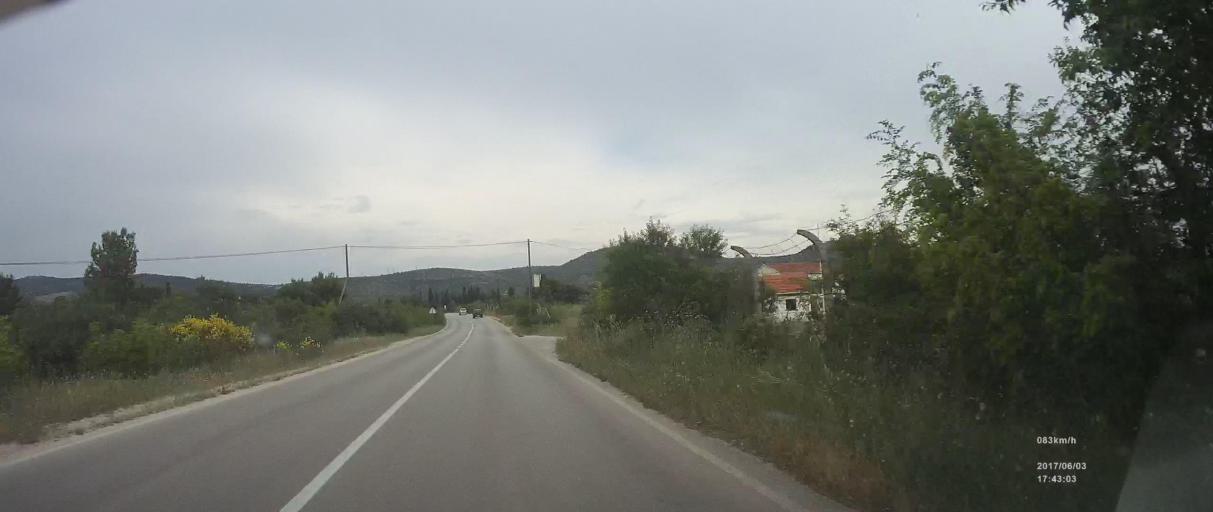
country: HR
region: Sibensko-Kniniska
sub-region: Grad Sibenik
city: Sibenik
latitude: 43.7119
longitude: 15.9028
